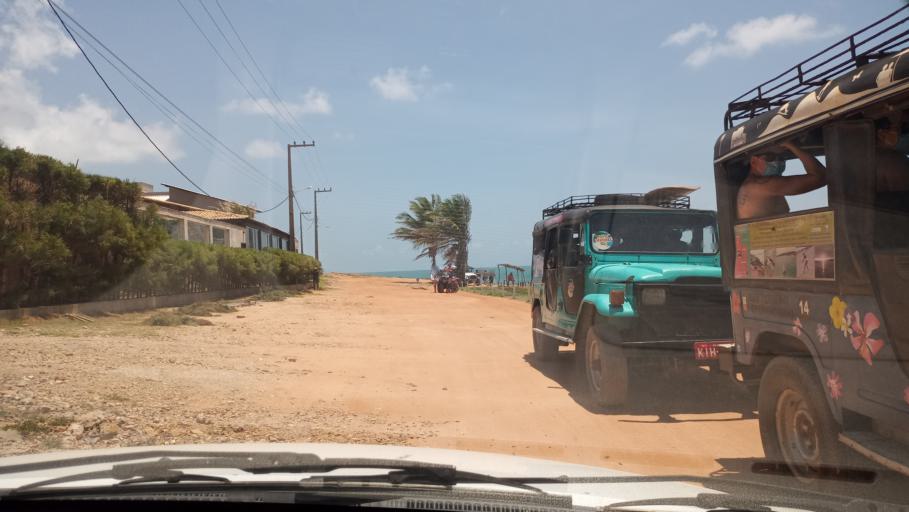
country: BR
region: Rio Grande do Norte
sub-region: Canguaretama
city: Canguaretama
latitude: -6.2778
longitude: -35.0352
